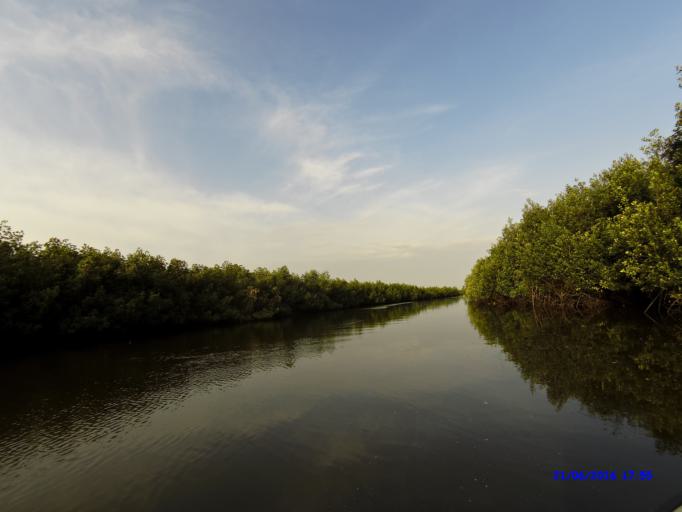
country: BJ
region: Mono
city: Come
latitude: 6.3099
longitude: 1.9541
